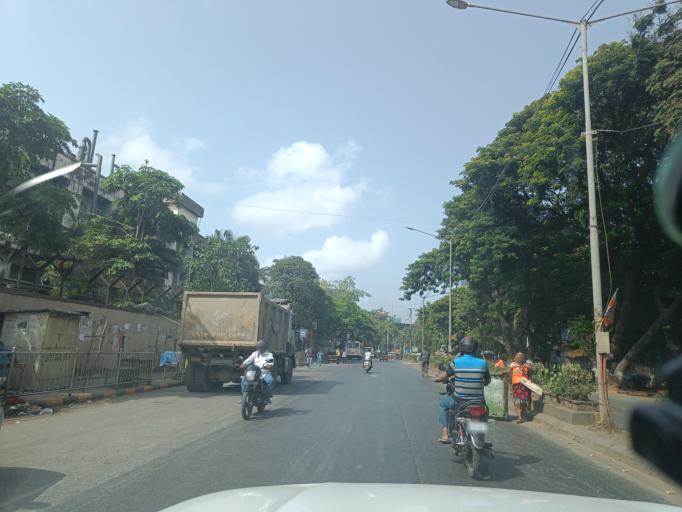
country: IN
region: Maharashtra
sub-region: Mumbai Suburban
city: Powai
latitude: 19.1241
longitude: 72.8722
